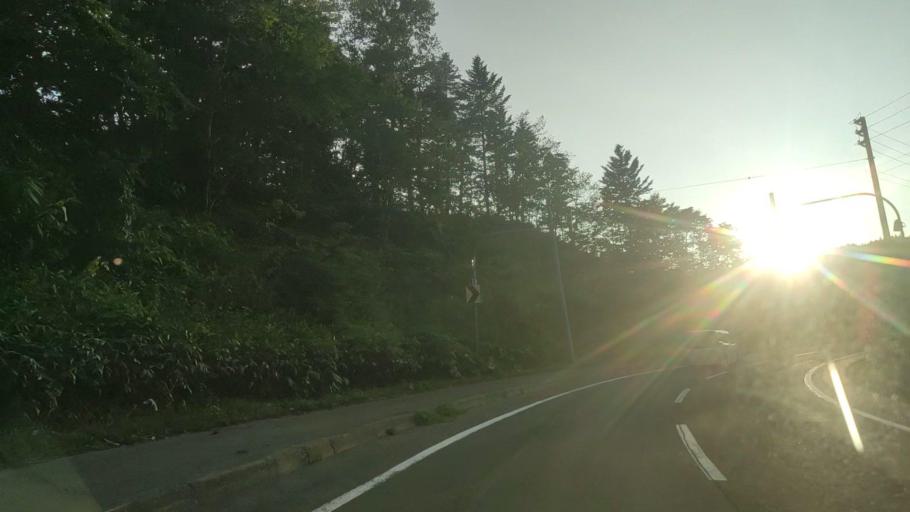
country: JP
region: Hokkaido
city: Bibai
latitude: 43.2362
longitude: 142.0311
